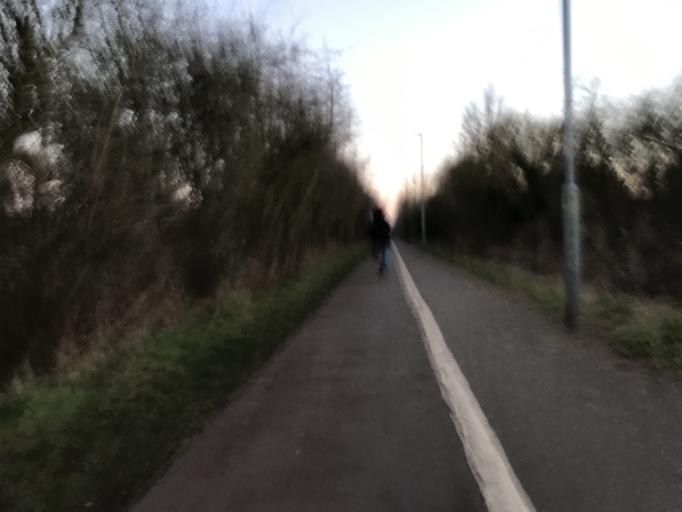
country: GB
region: England
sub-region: Lincolnshire
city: Holton le Clay
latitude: 53.5278
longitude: -0.0652
